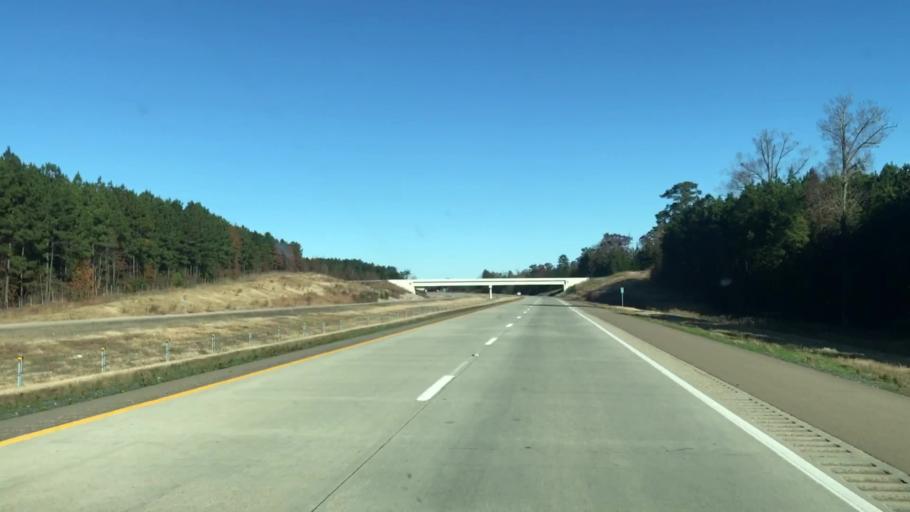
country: US
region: Louisiana
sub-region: Caddo Parish
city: Vivian
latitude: 33.0478
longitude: -93.9007
